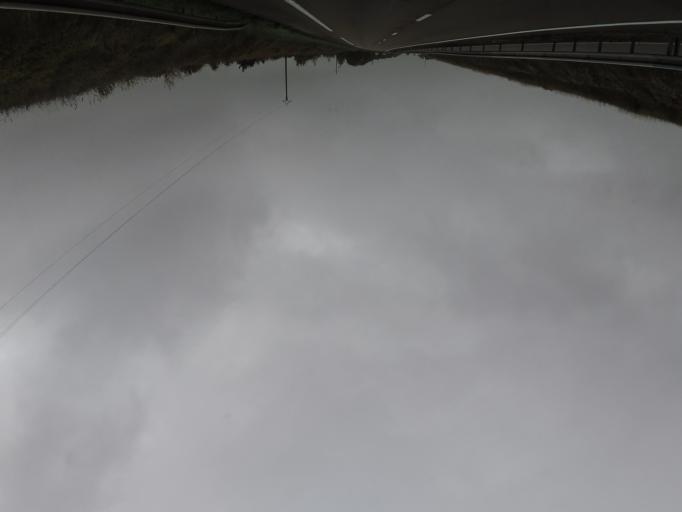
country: FR
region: Champagne-Ardenne
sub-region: Departement de la Marne
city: Verzy
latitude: 49.1331
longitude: 4.2223
